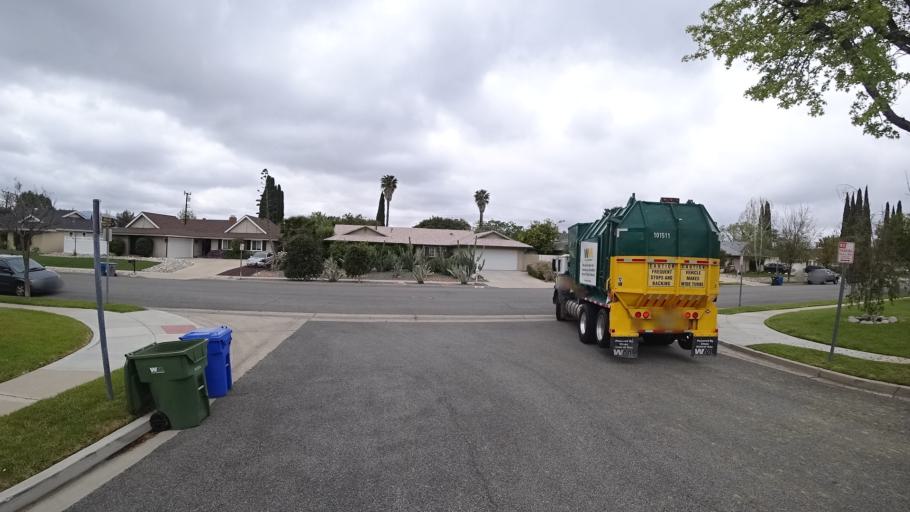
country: US
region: California
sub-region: Ventura County
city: Thousand Oaks
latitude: 34.2113
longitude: -118.8733
